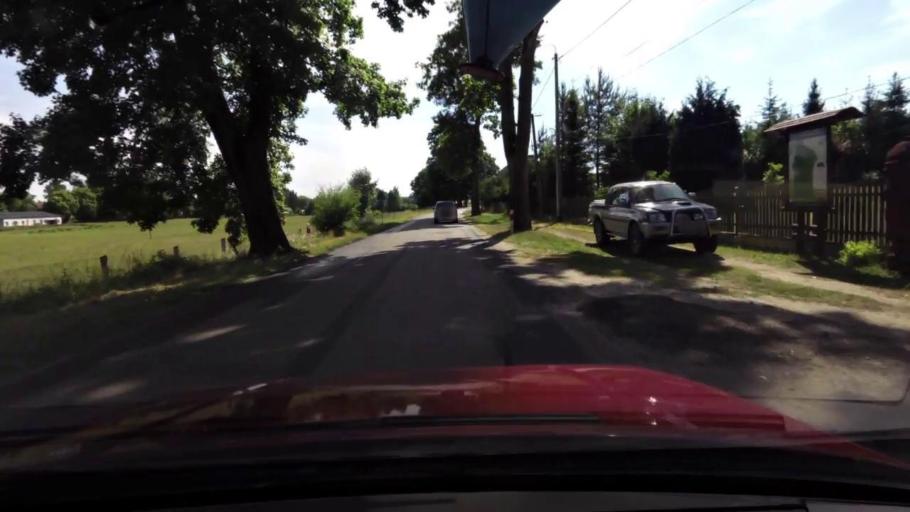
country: PL
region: Pomeranian Voivodeship
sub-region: Powiat slupski
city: Kepice
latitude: 54.2578
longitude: 16.9414
